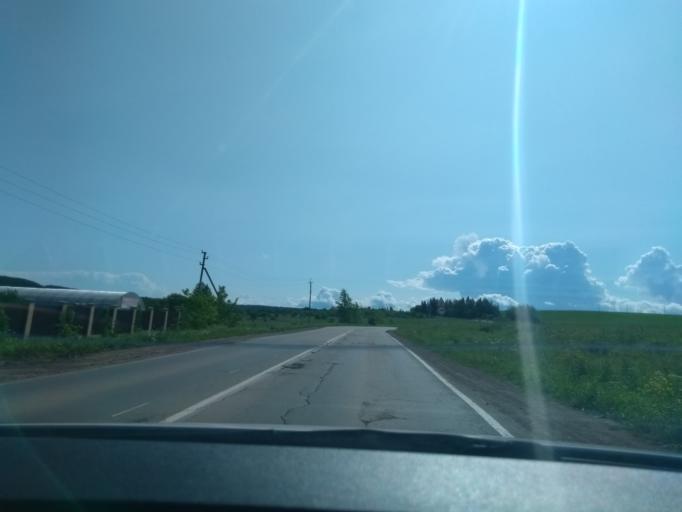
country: RU
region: Perm
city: Lobanovo
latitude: 57.8547
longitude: 56.3212
